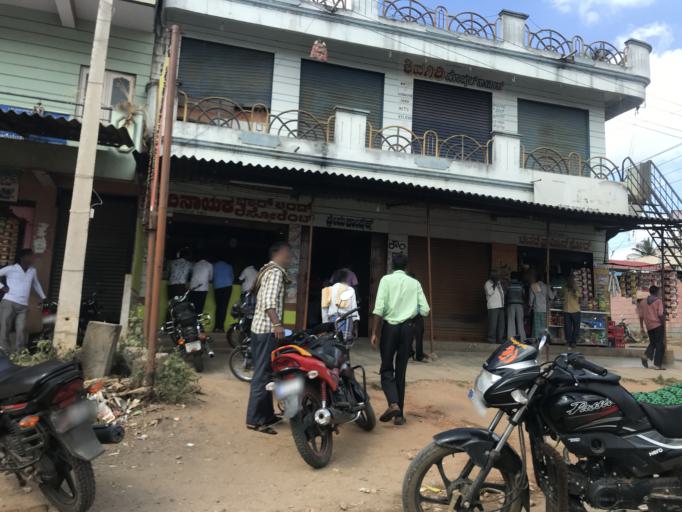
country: IN
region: Karnataka
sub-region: Mandya
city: Krishnarajpet
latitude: 12.7608
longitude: 76.4240
